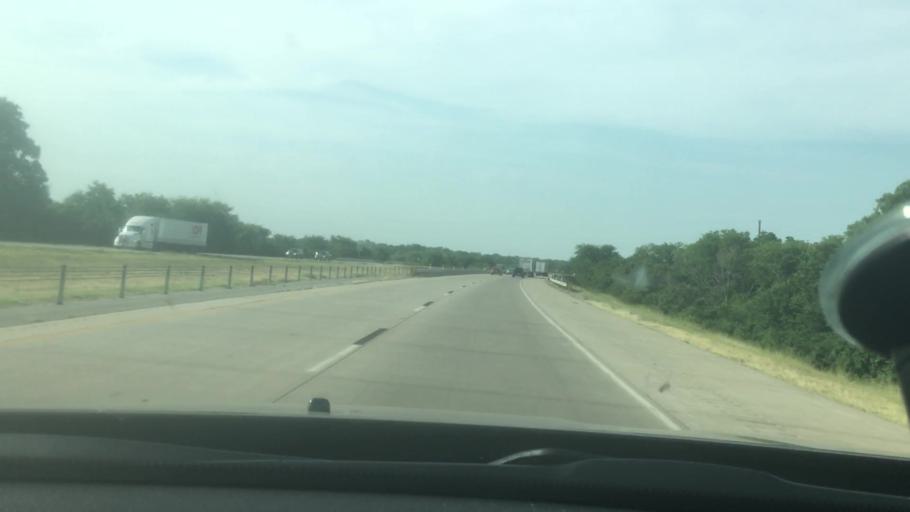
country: US
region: Oklahoma
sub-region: Murray County
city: Davis
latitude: 34.3494
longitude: -97.1481
